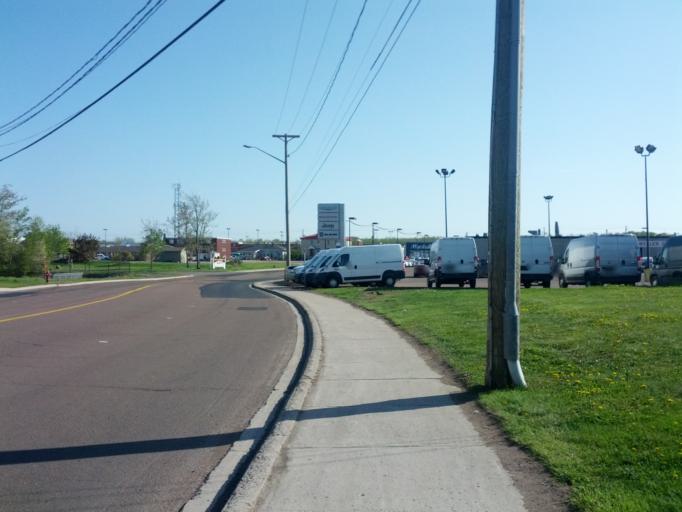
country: CA
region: New Brunswick
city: Moncton
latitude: 46.1128
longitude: -64.8308
